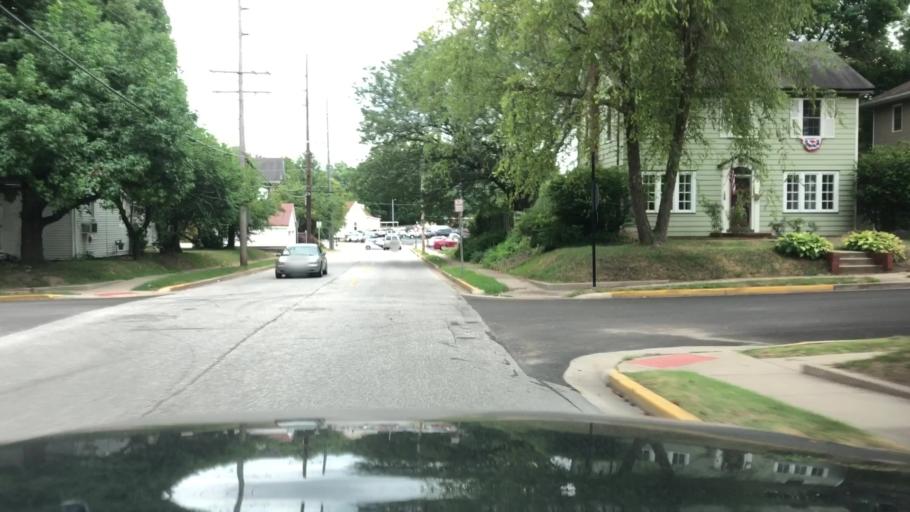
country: US
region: Missouri
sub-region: Saint Charles County
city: Saint Charles
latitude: 38.7875
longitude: -90.4952
